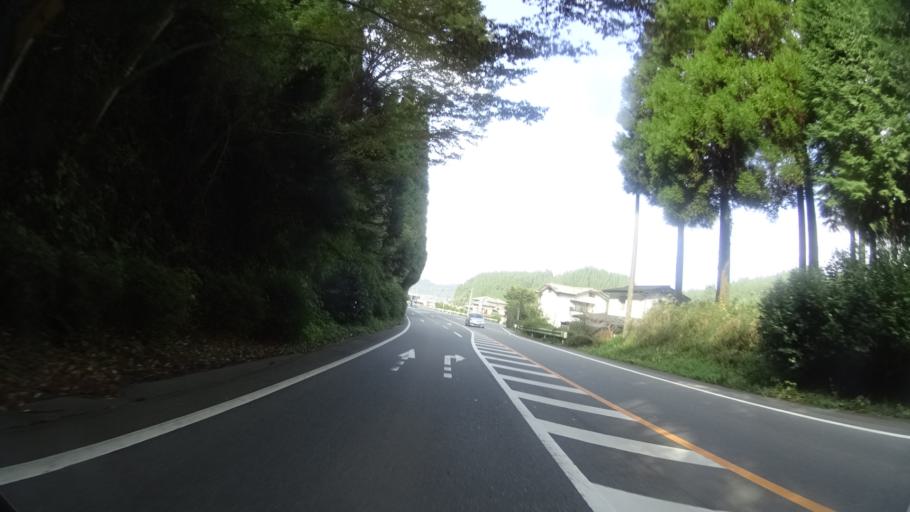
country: JP
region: Kumamoto
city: Aso
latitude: 33.0879
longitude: 131.0677
